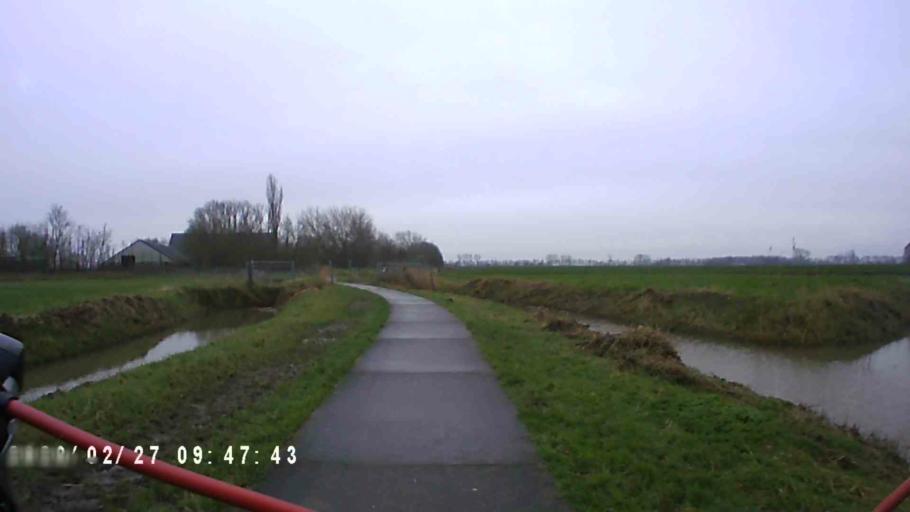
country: NL
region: Groningen
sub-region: Gemeente Zuidhorn
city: Aduard
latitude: 53.2731
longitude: 6.4490
